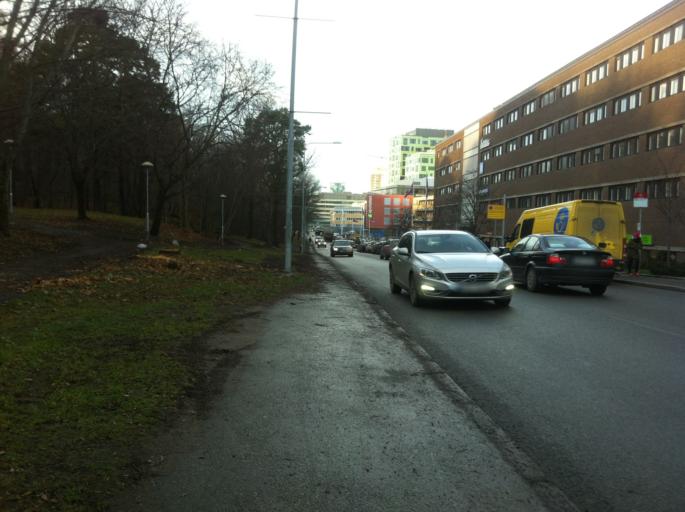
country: SE
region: Stockholm
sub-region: Solna Kommun
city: Solna
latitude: 59.3663
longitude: 18.0069
